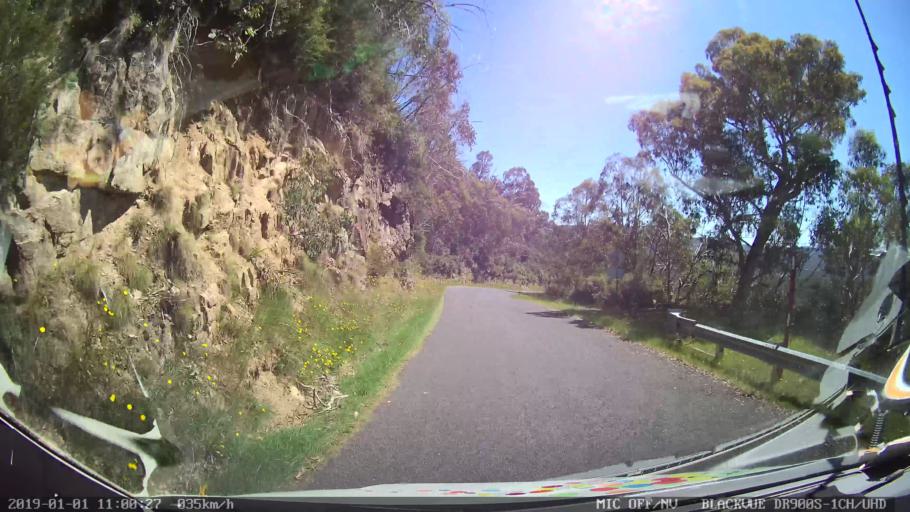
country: AU
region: New South Wales
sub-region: Snowy River
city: Jindabyne
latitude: -35.9806
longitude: 148.3973
